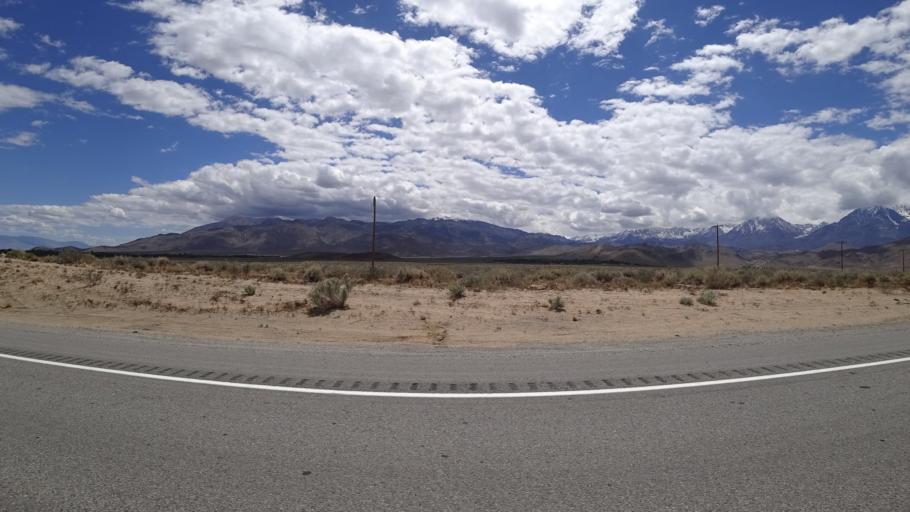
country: US
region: California
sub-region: Inyo County
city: West Bishop
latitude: 37.3769
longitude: -118.4671
